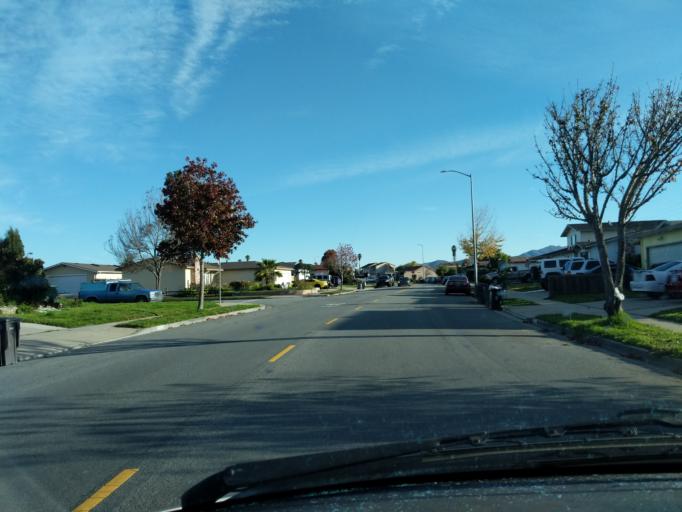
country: US
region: California
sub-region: Monterey County
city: Boronda
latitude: 36.7068
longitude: -121.6614
